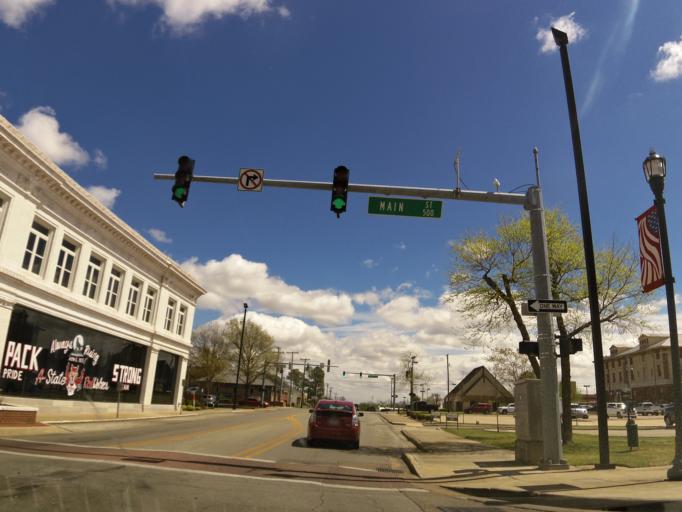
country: US
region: Arkansas
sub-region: Craighead County
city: Jonesboro
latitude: 35.8383
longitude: -90.7049
